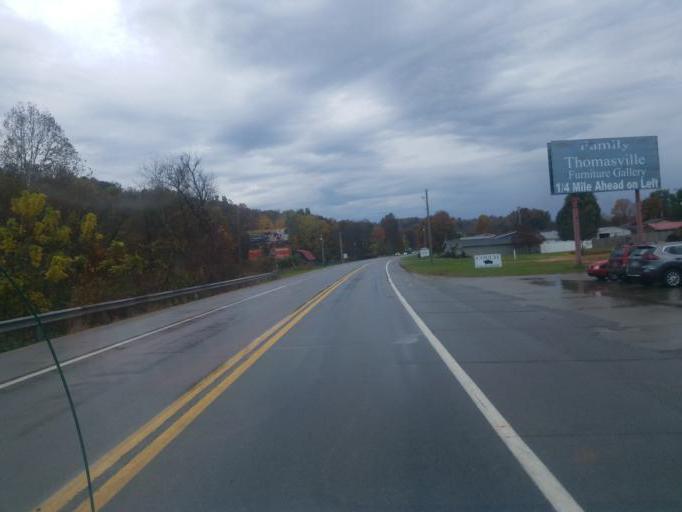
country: US
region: West Virginia
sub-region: Wood County
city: Boaz
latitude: 39.3690
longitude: -81.4833
